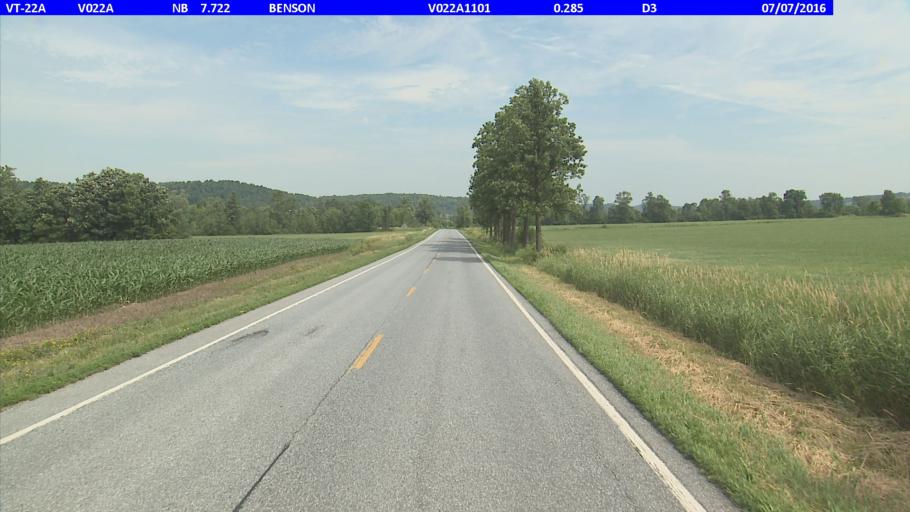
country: US
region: Vermont
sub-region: Rutland County
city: Fair Haven
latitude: 43.6734
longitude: -73.2890
